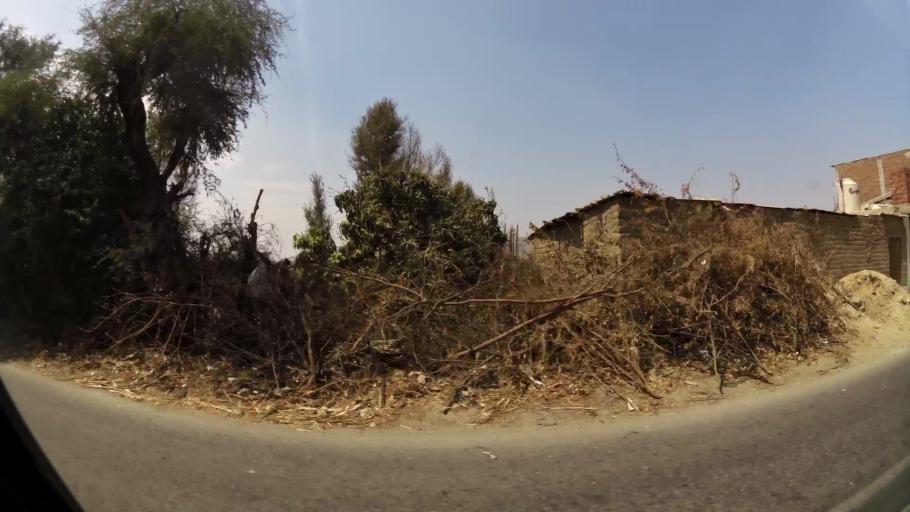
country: PE
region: La Libertad
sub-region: Chepen
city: Chepen
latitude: -7.2029
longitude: -79.4277
